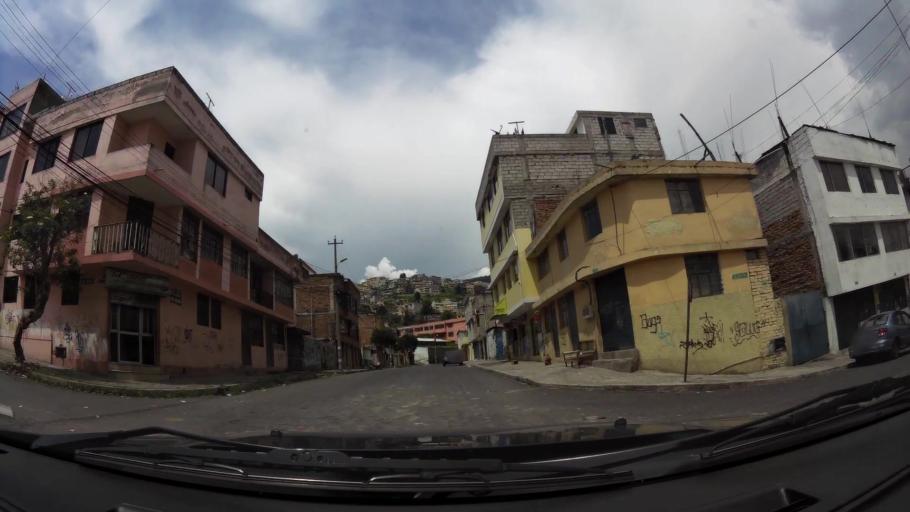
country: EC
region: Pichincha
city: Quito
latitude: -0.2574
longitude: -78.5213
